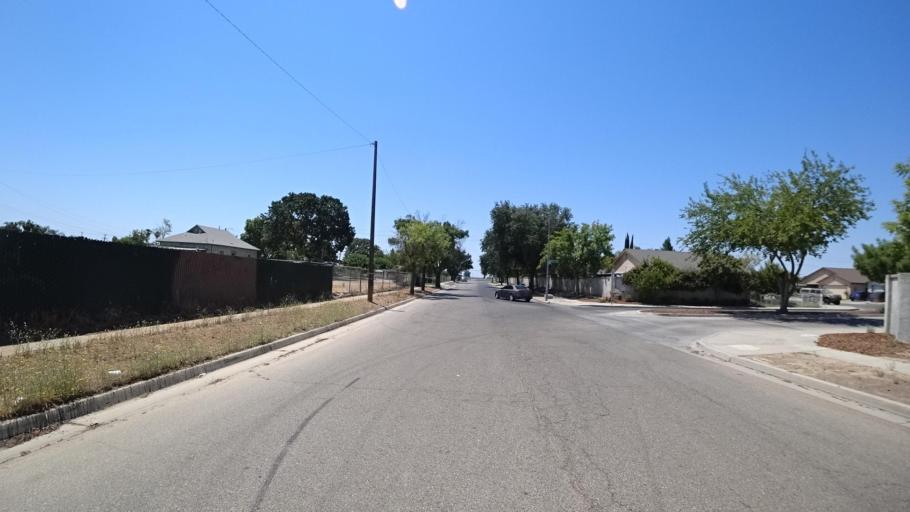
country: US
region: California
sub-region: Fresno County
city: West Park
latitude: 36.7084
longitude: -119.8157
